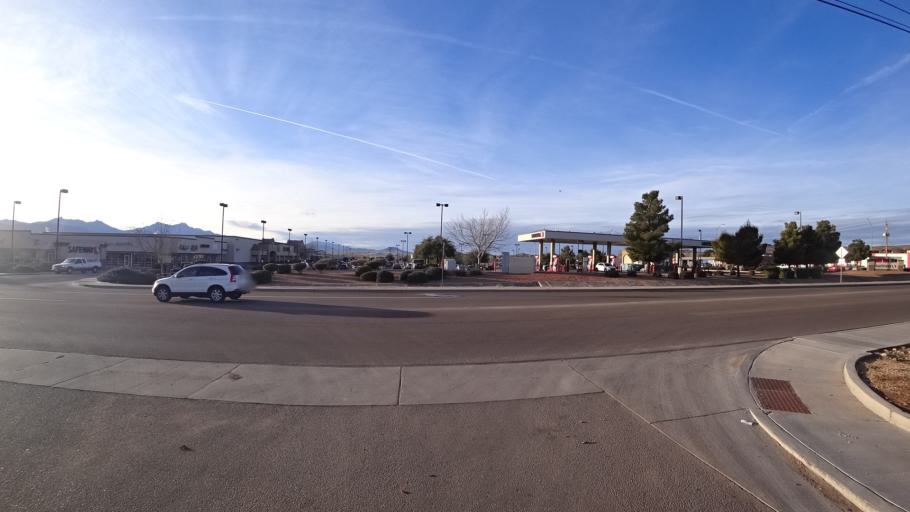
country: US
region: Arizona
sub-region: Mohave County
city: New Kingman-Butler
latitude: 35.2395
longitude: -114.0368
